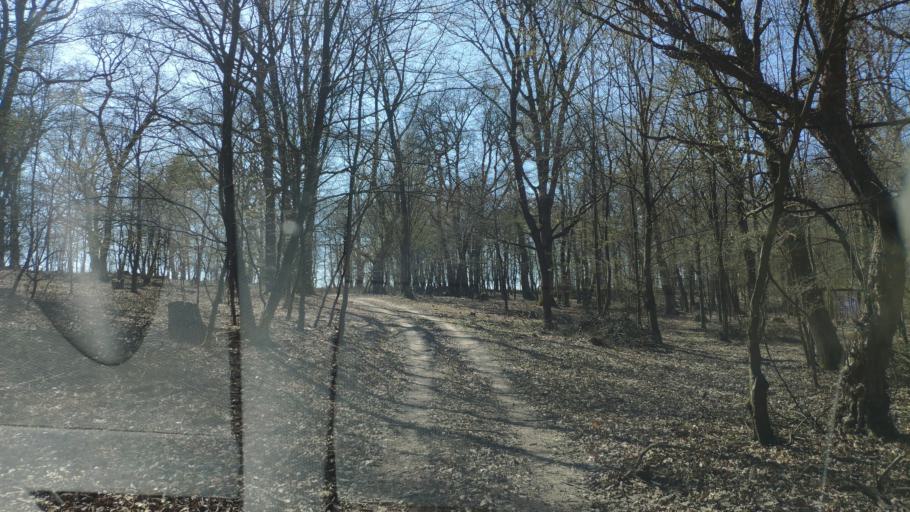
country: SK
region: Kosicky
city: Moldava nad Bodvou
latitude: 48.5647
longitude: 20.9311
